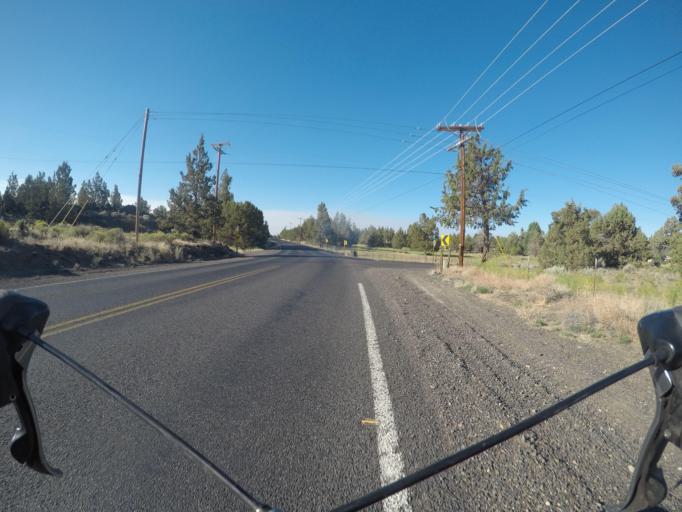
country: US
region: Oregon
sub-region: Deschutes County
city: Redmond
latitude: 44.1963
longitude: -121.2440
